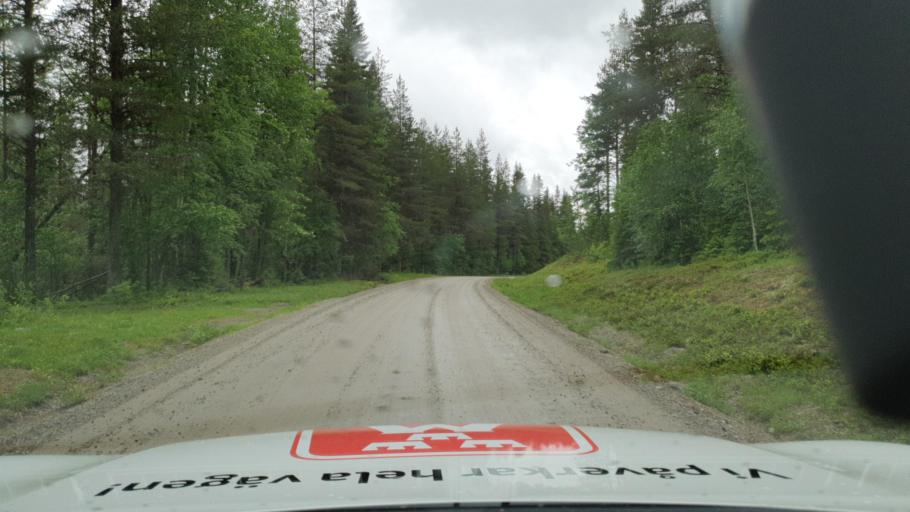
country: SE
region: Vaesterbotten
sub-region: Dorotea Kommun
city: Dorotea
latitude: 64.0471
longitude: 16.7330
